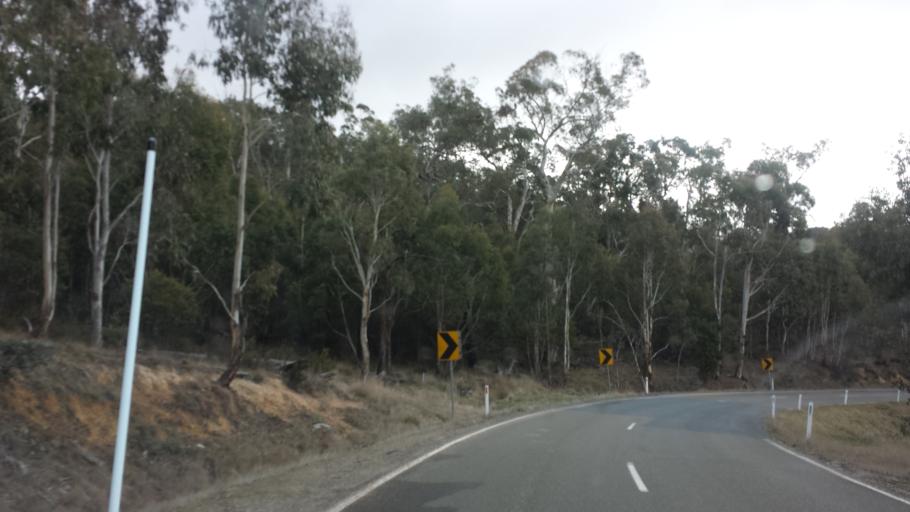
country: AU
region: Victoria
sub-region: Alpine
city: Mount Beauty
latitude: -37.1255
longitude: 147.5379
